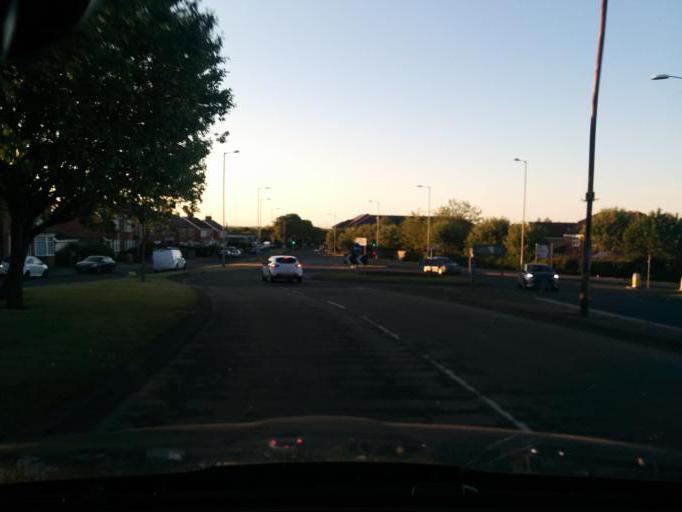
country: GB
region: England
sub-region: Northumberland
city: Bedlington
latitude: 55.1330
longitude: -1.5997
